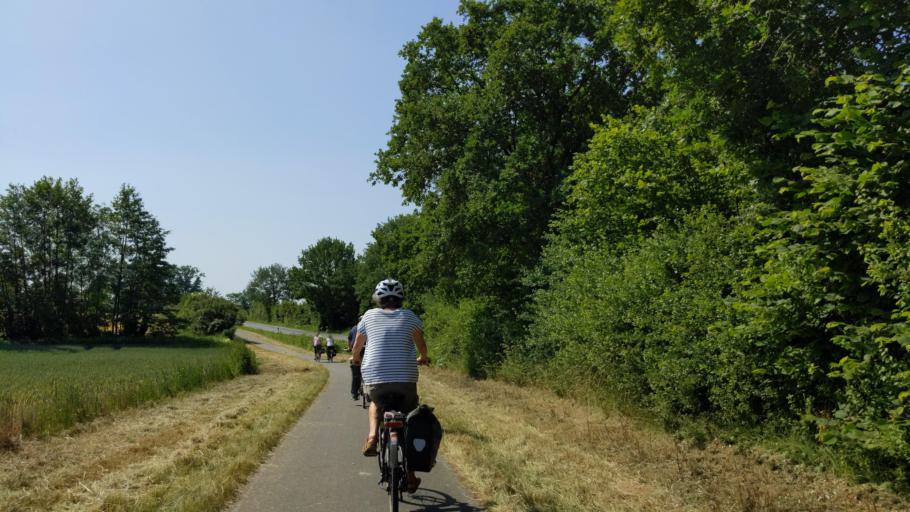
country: DE
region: Schleswig-Holstein
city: Klempau
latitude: 53.7540
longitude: 10.6573
